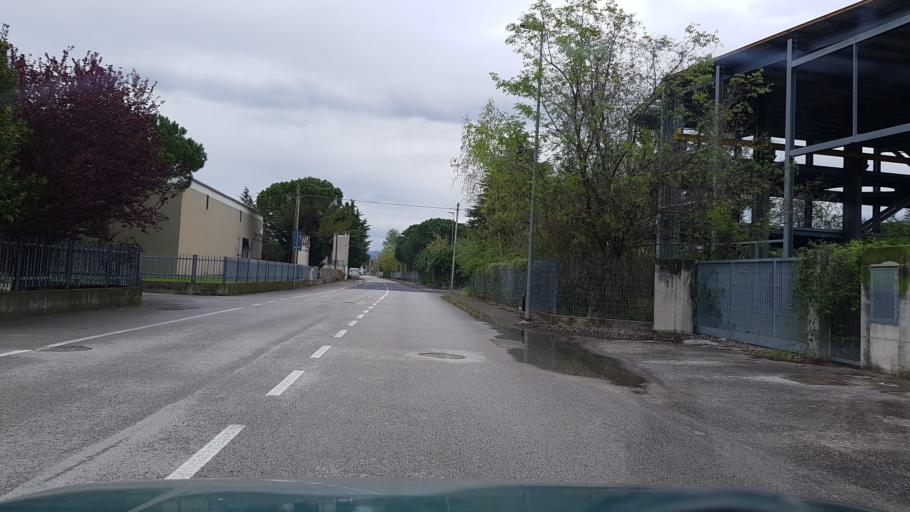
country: IT
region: Friuli Venezia Giulia
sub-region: Provincia di Gorizia
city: Mossa
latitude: 45.9298
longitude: 13.5485
